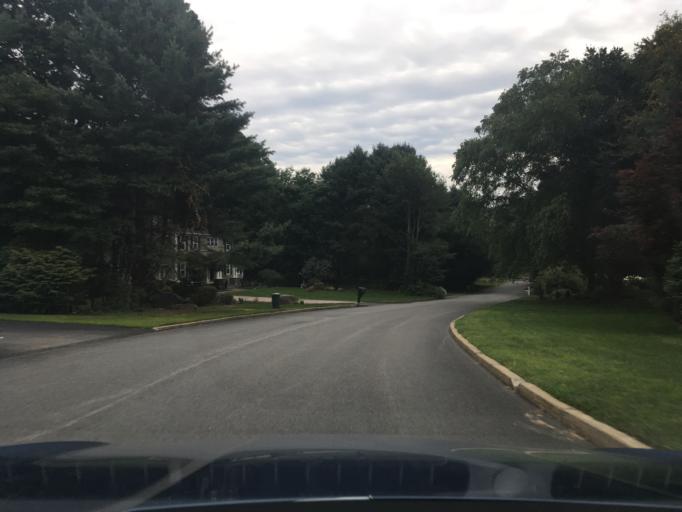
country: US
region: Rhode Island
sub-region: Kent County
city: East Greenwich
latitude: 41.6341
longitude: -71.5020
